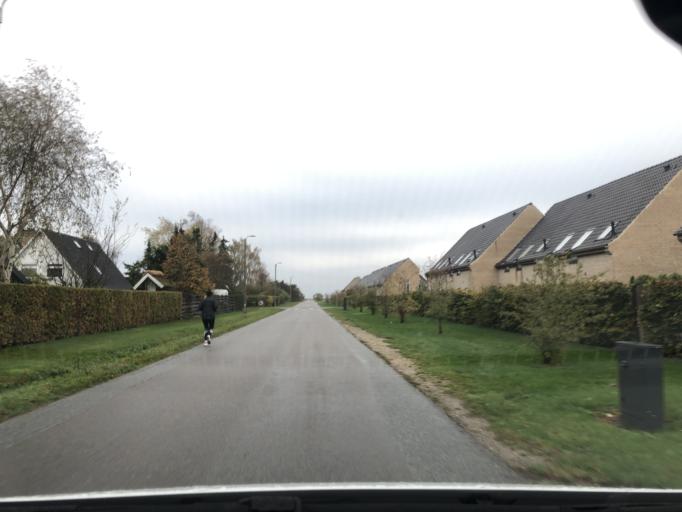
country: DK
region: Capital Region
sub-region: Dragor Kommune
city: Dragor
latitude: 55.5824
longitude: 12.6395
